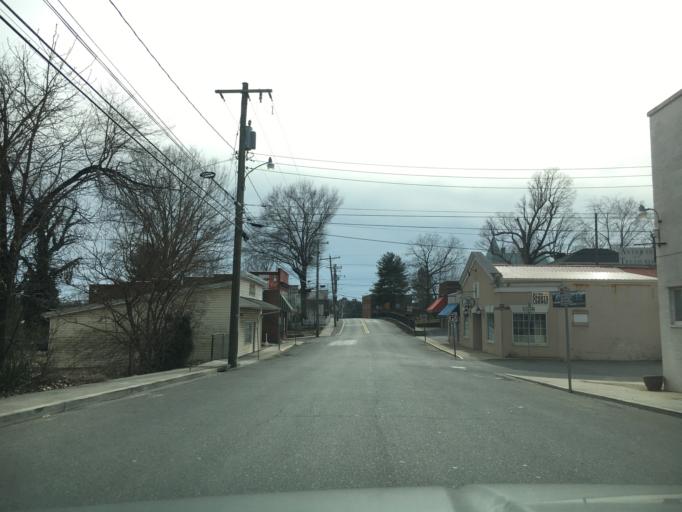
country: US
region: Virginia
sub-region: Appomattox County
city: Appomattox
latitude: 37.3554
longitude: -78.8262
